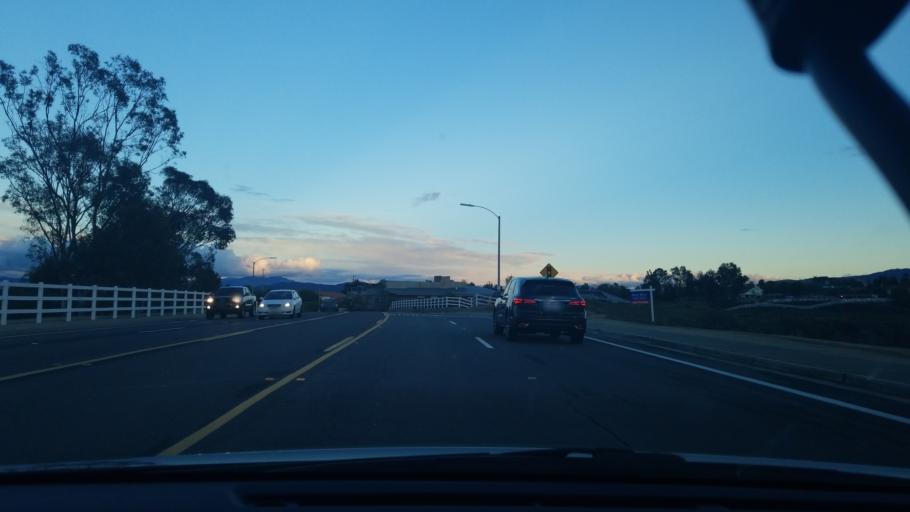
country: US
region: California
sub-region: Riverside County
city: Temecula
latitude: 33.4971
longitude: -117.1187
